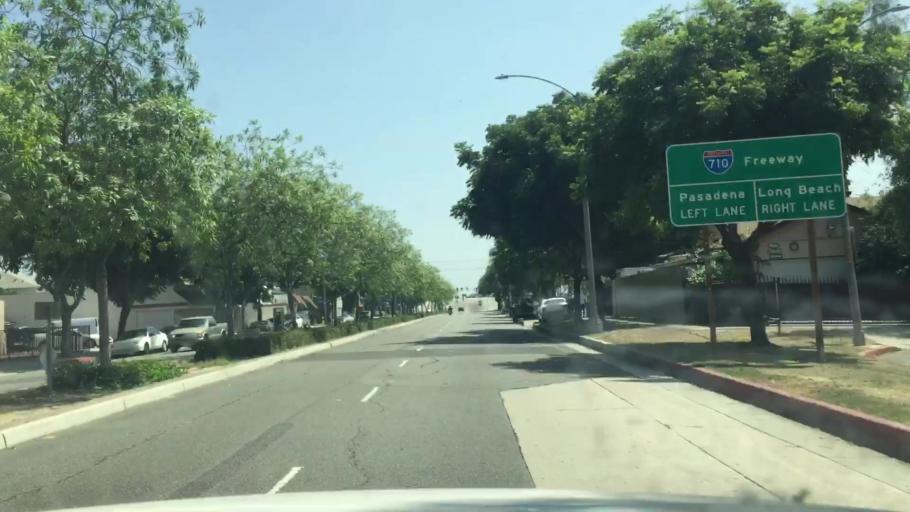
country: US
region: California
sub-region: Los Angeles County
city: East Rancho Dominguez
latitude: 33.8673
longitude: -118.2007
